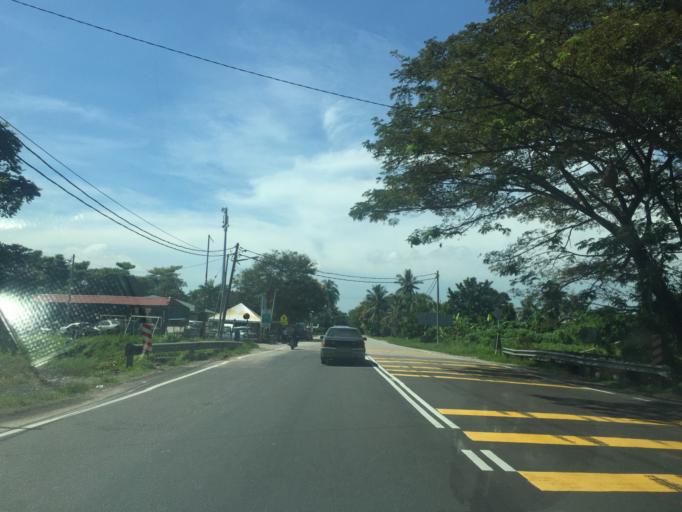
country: MY
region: Penang
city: Tasek Glugor
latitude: 5.4690
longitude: 100.4567
